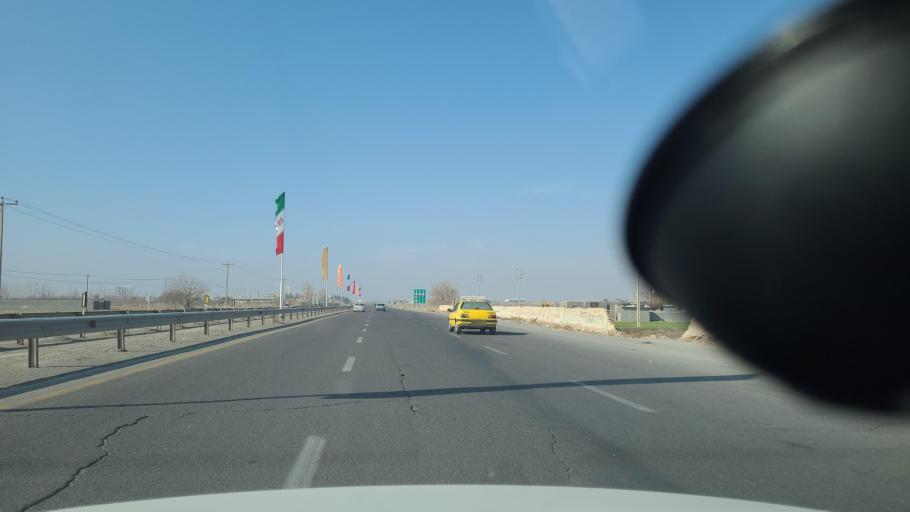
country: IR
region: Razavi Khorasan
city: Fariman
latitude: 35.7083
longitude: 59.8333
